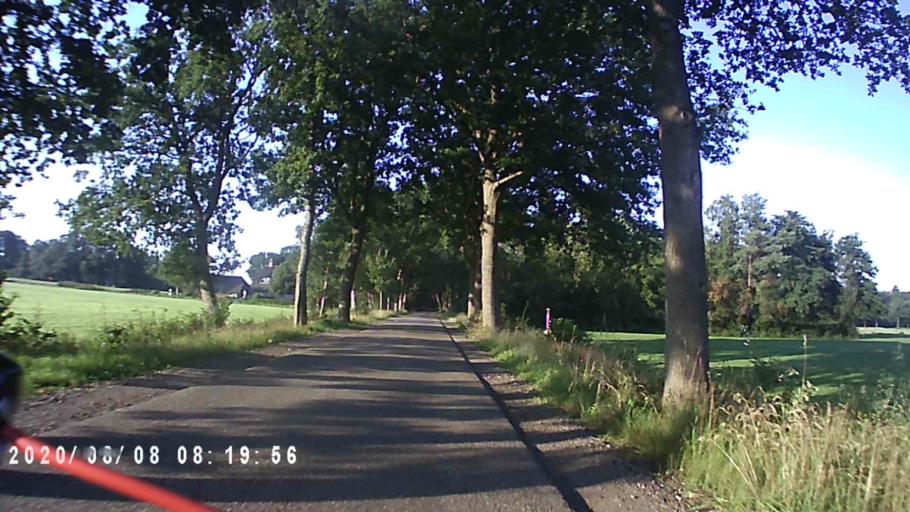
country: NL
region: Groningen
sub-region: Gemeente Leek
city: Leek
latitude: 53.0951
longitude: 6.3150
